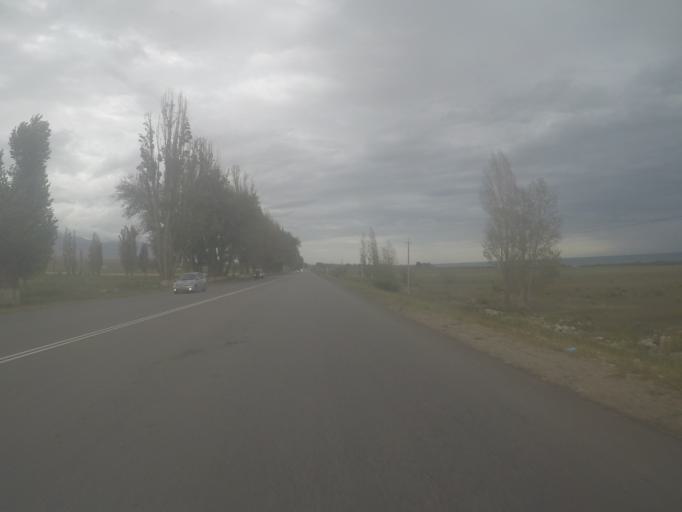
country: KG
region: Ysyk-Koel
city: Cholpon-Ata
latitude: 42.5962
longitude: 76.7740
